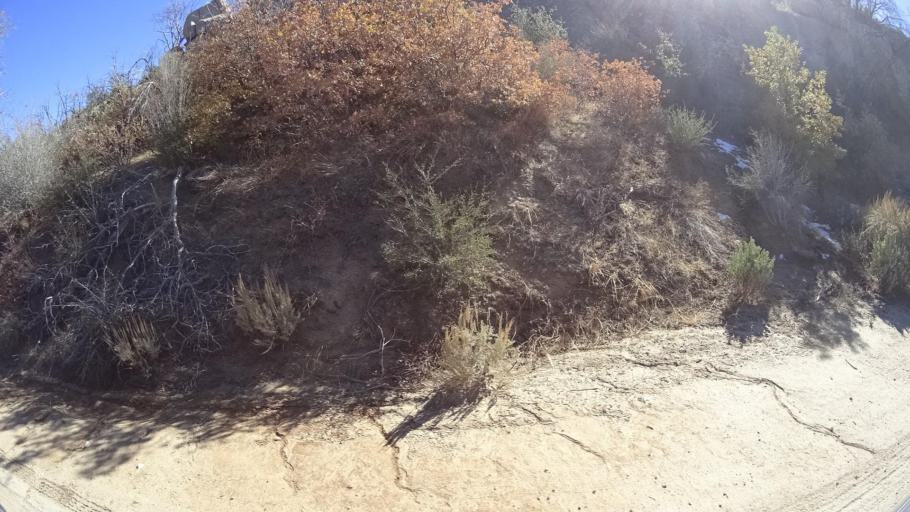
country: US
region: California
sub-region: Kern County
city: Alta Sierra
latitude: 35.7101
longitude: -118.5142
